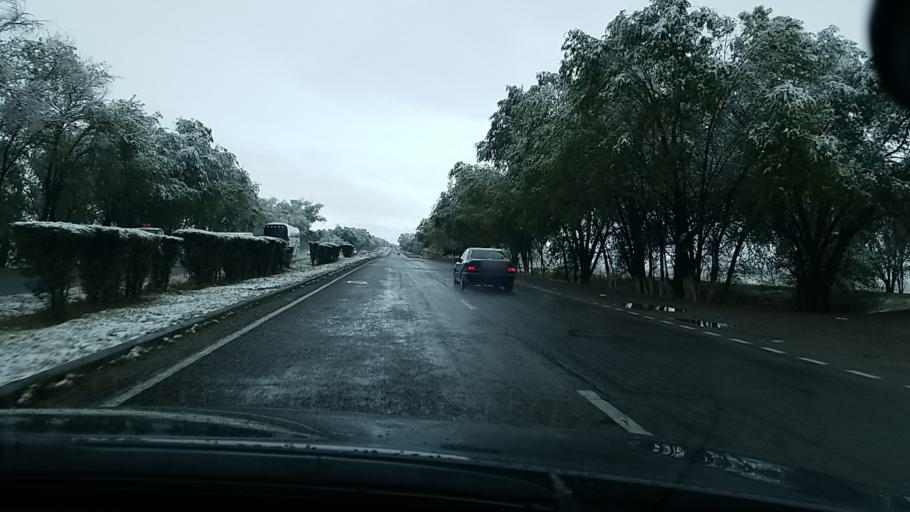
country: KZ
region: Almaty Oblysy
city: Burunday
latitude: 43.2204
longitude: 76.4642
